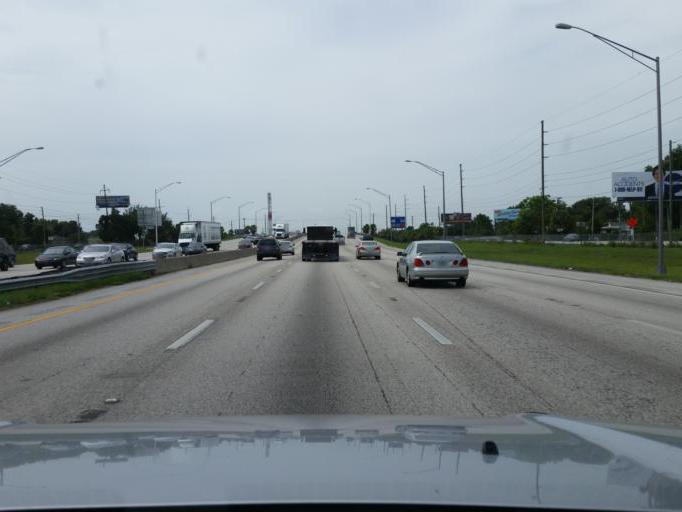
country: US
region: Florida
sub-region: Orange County
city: Eatonville
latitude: 28.6222
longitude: -81.3867
